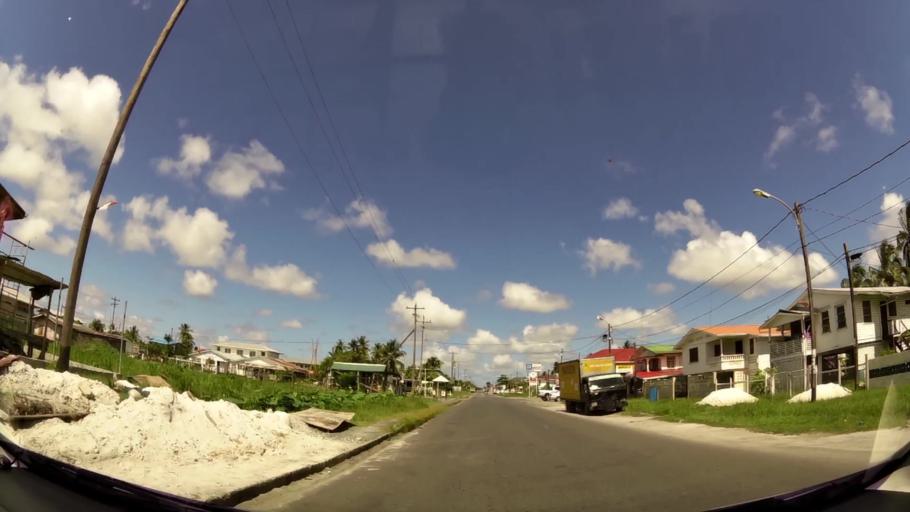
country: GY
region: Demerara-Mahaica
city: Georgetown
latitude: 6.7852
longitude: -58.1362
